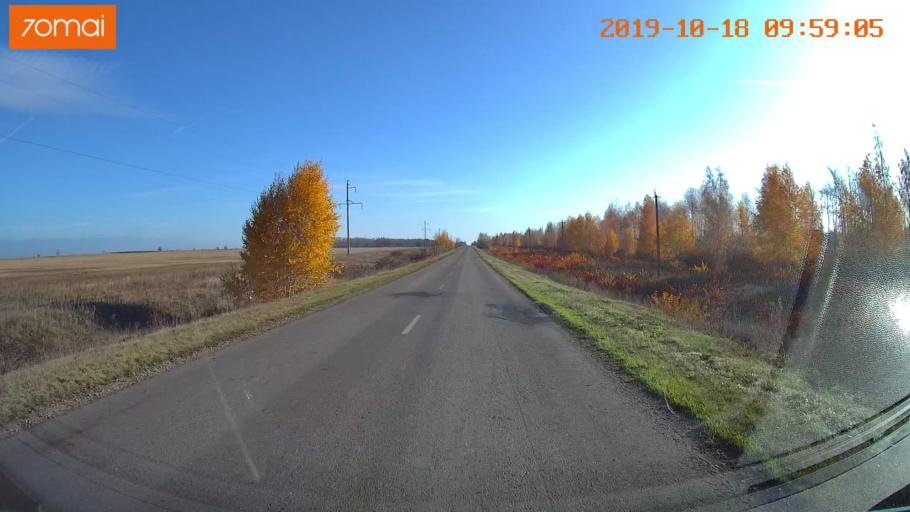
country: RU
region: Tula
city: Kurkino
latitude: 53.3766
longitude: 38.4545
